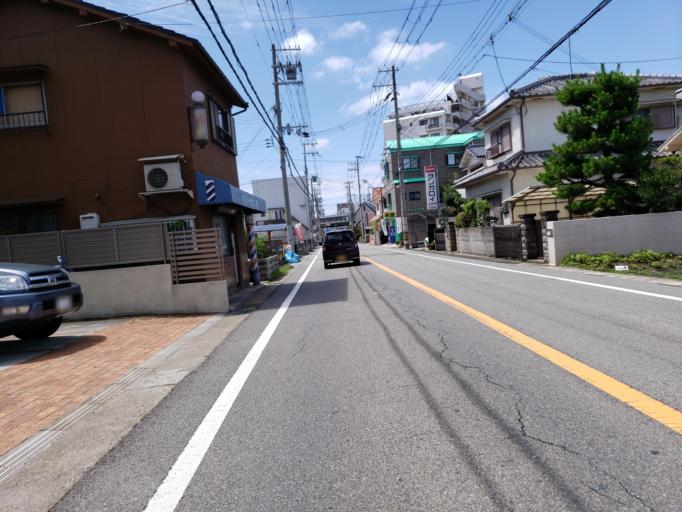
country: JP
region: Hyogo
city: Kakogawacho-honmachi
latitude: 34.7053
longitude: 134.8905
